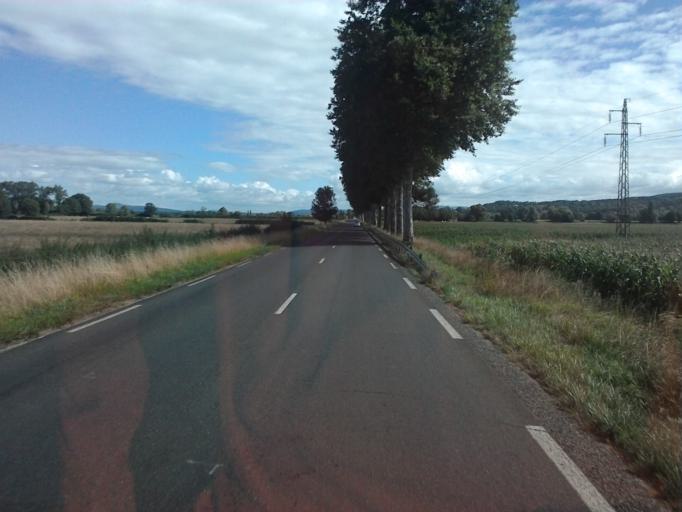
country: FR
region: Rhone-Alpes
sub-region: Departement de l'Ain
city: Ambronay
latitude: 45.9876
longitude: 5.3503
